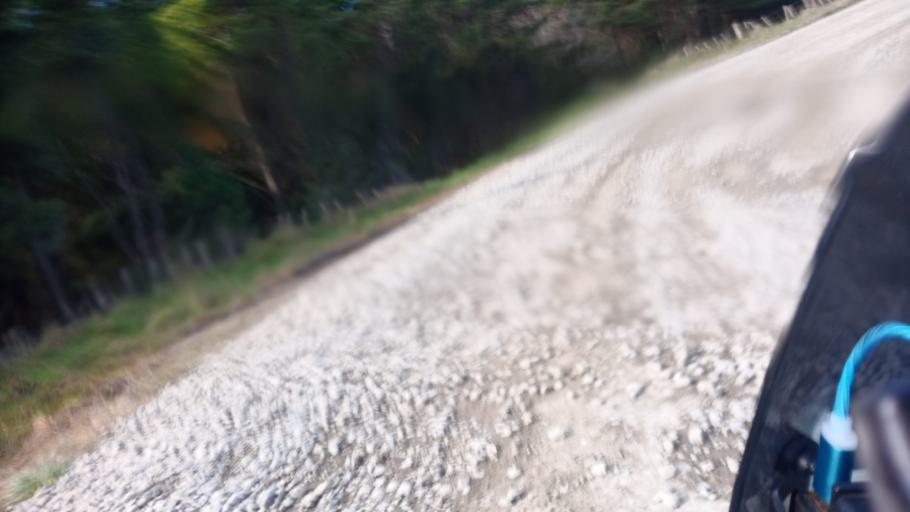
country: NZ
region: Gisborne
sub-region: Gisborne District
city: Gisborne
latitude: -38.1295
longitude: 178.1792
